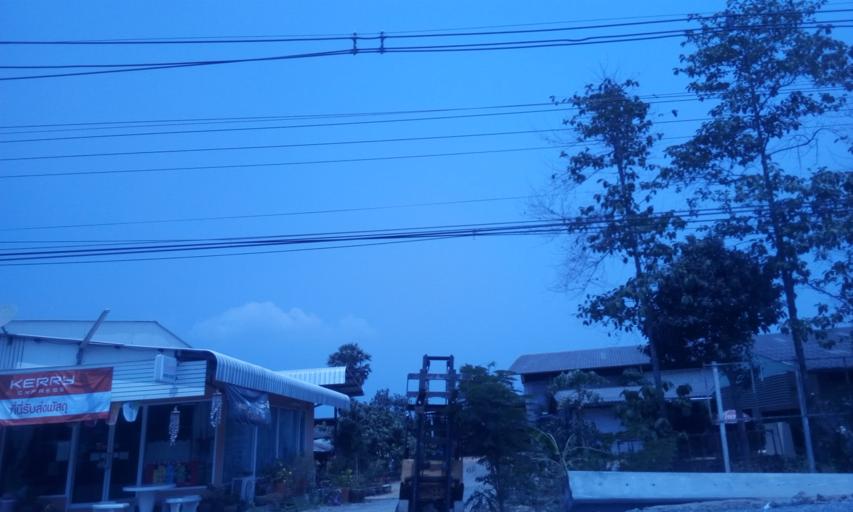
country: TH
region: Chachoengsao
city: Ban Pho
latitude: 13.5524
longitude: 101.1397
